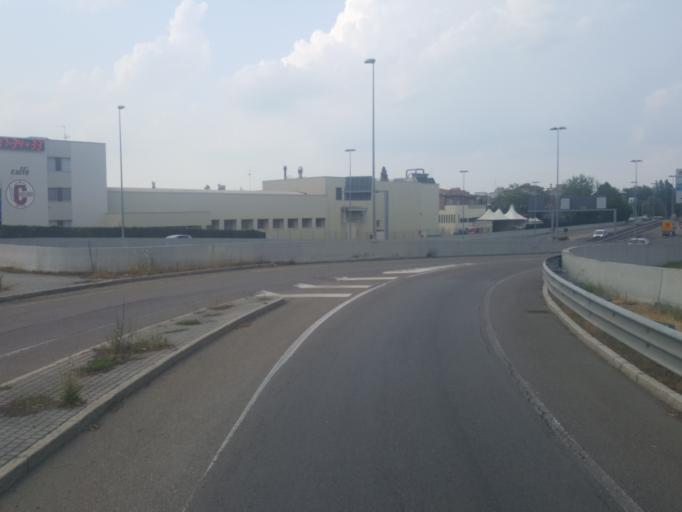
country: IT
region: Emilia-Romagna
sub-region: Provincia di Modena
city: Modena
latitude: 44.6331
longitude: 10.9575
